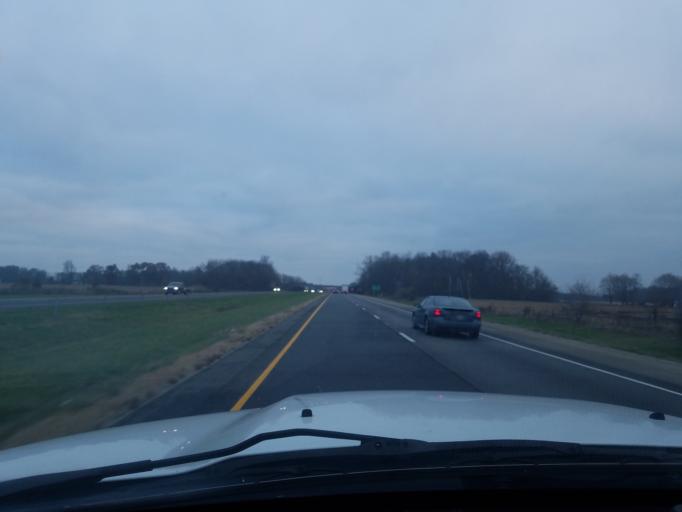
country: US
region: Indiana
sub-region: Delaware County
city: Daleville
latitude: 40.1299
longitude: -85.5683
